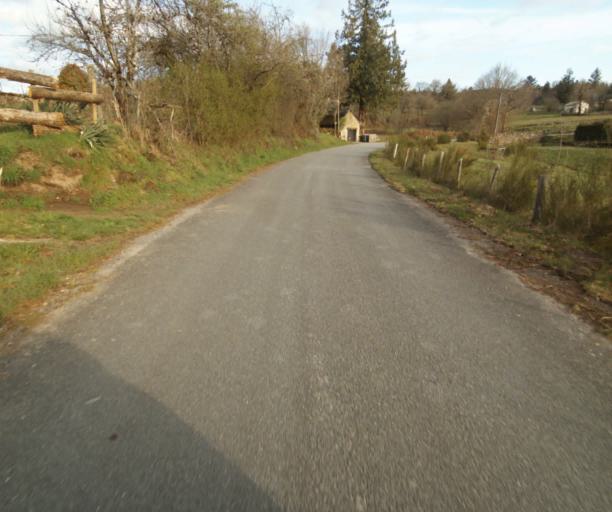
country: FR
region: Limousin
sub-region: Departement de la Correze
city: Correze
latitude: 45.4023
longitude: 1.9001
